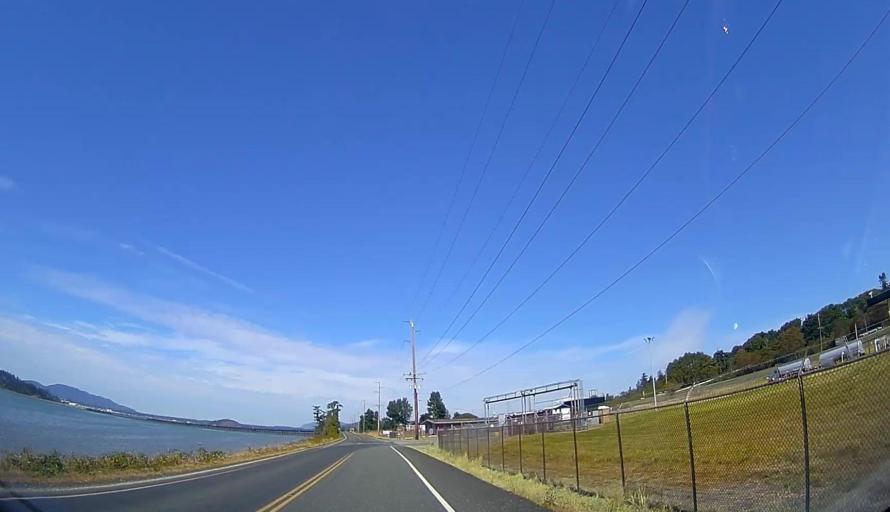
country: US
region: Washington
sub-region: Skagit County
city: Anacortes
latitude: 48.4722
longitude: -122.5711
